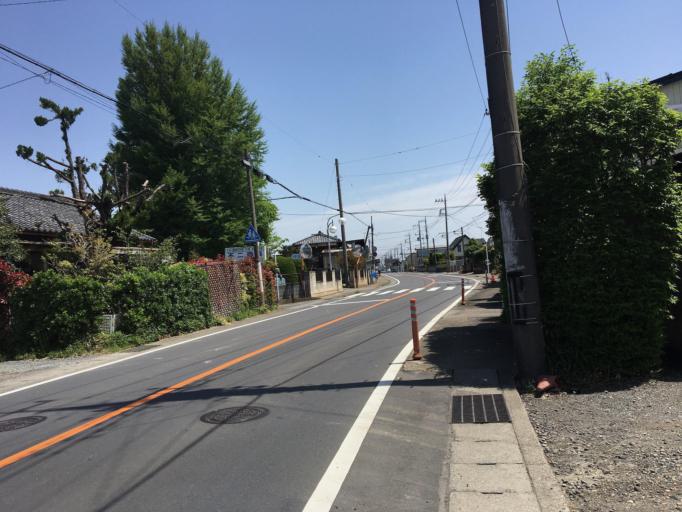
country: JP
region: Gunma
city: Sakai-nakajima
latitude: 36.2797
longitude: 139.3003
